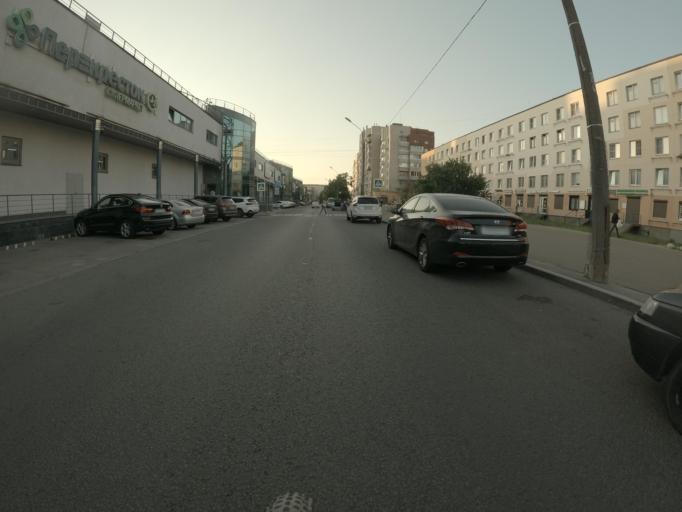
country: RU
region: St.-Petersburg
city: Dachnoye
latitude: 59.8492
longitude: 30.2689
